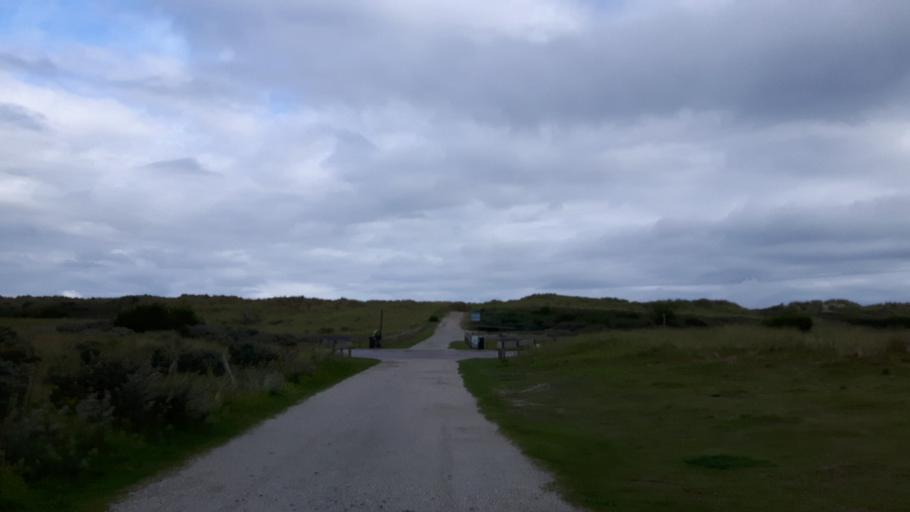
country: NL
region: Friesland
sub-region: Gemeente Ameland
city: Nes
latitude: 53.4572
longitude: 5.7581
